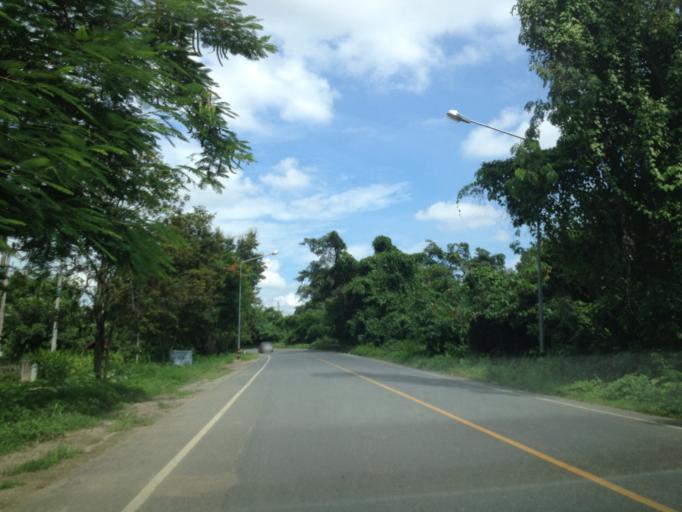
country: TH
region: Chiang Mai
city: Hang Dong
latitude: 18.7371
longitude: 98.8996
